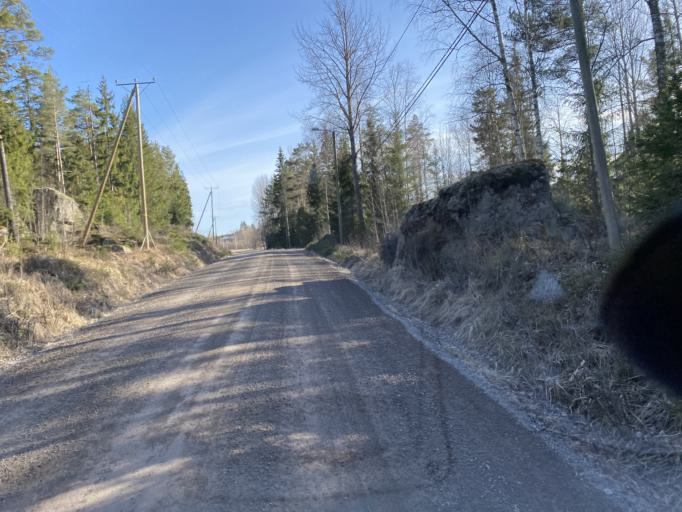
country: FI
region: Satakunta
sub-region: Rauma
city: Lappi
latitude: 61.1337
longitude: 21.9488
